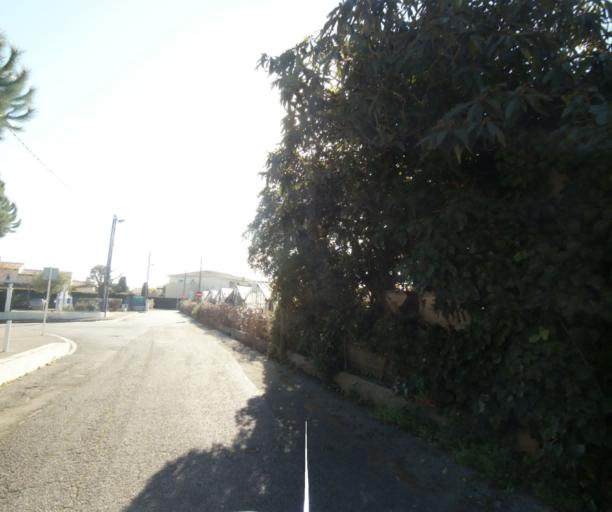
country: FR
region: Provence-Alpes-Cote d'Azur
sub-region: Departement des Alpes-Maritimes
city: Biot
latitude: 43.6071
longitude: 7.1157
